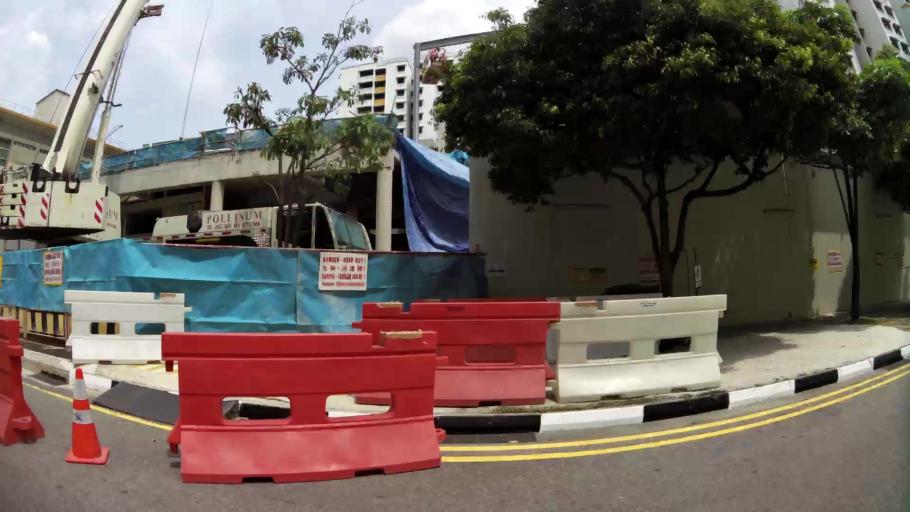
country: MY
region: Johor
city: Johor Bahru
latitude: 1.3410
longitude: 103.6972
